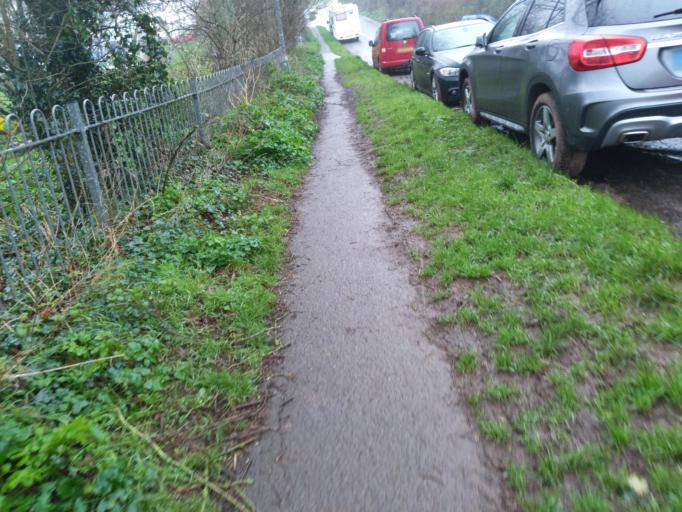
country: GB
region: England
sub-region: Cornwall
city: Millbrook
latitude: 50.3370
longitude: -4.2044
